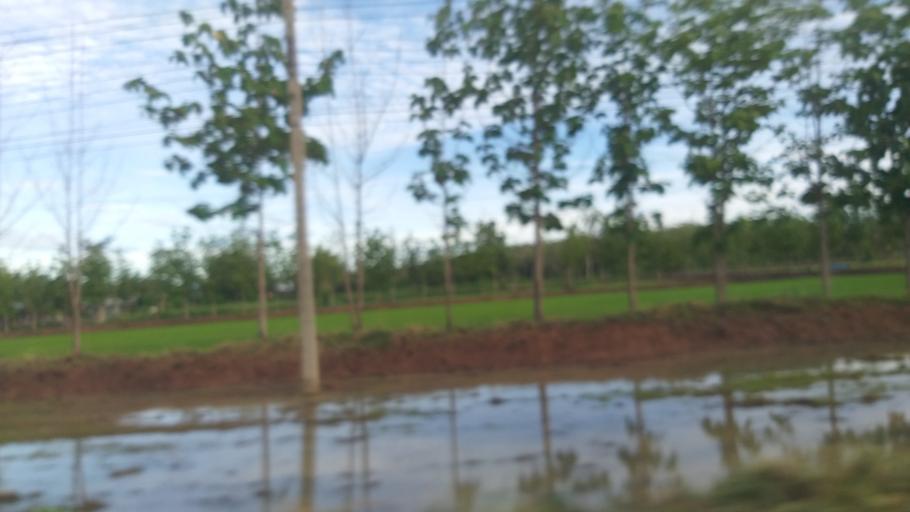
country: TH
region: Chaiyaphum
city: Phu Khiao
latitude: 16.3434
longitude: 102.2382
